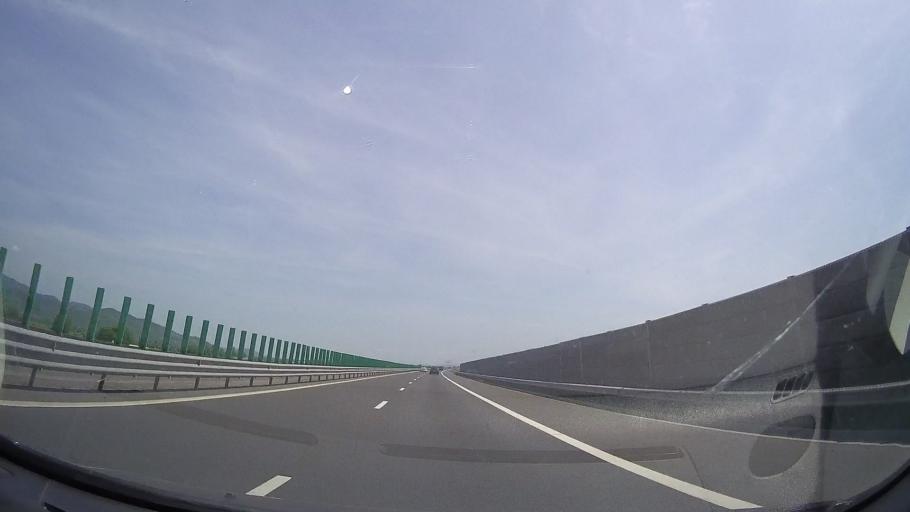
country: RO
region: Alba
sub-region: Comuna Sibot
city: Sibot
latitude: 45.9234
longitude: 23.3429
